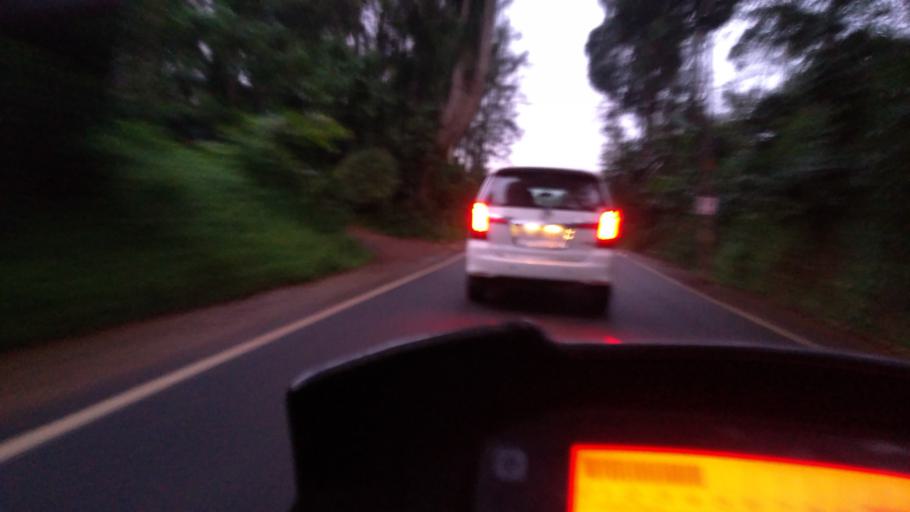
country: IN
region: Kerala
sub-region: Idukki
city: Munnar
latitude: 9.9586
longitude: 77.0865
